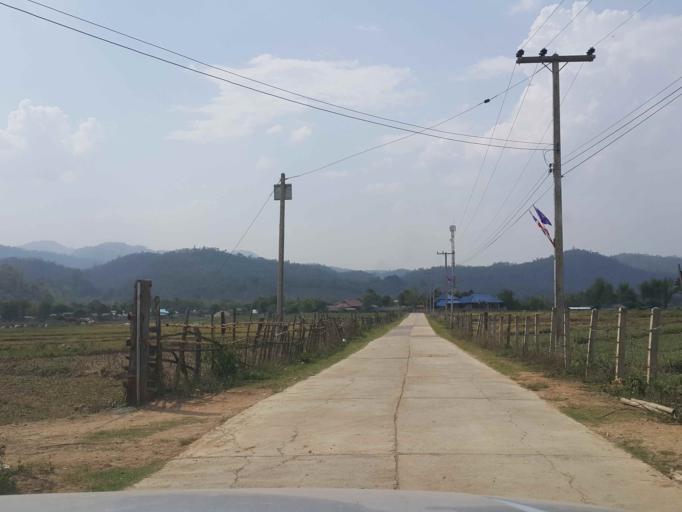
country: TH
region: Chiang Mai
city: Wiang Haeng
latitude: 19.3809
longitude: 98.7189
